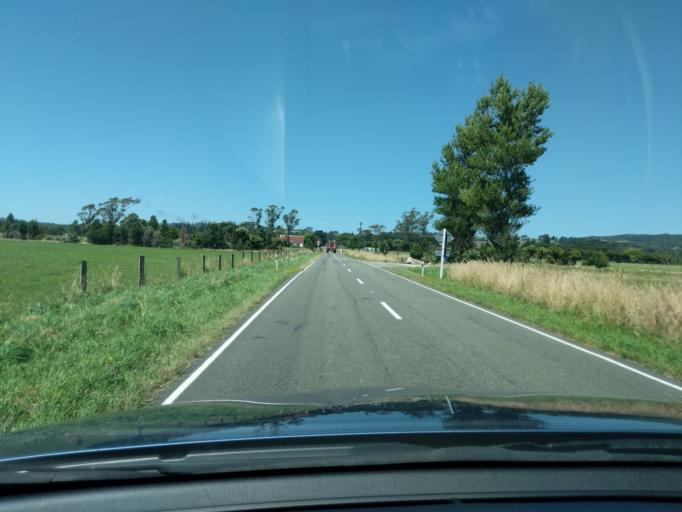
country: NZ
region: Tasman
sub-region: Tasman District
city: Takaka
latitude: -40.7298
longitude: 172.6143
